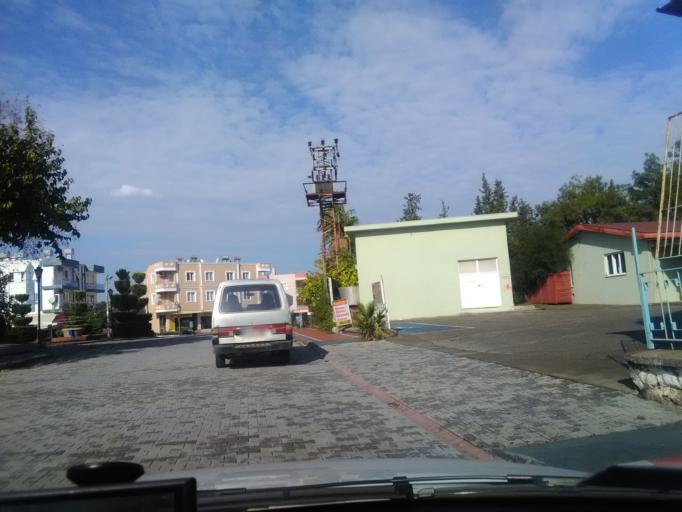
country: TR
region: Antalya
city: Gazipasa
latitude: 36.2712
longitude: 32.3087
